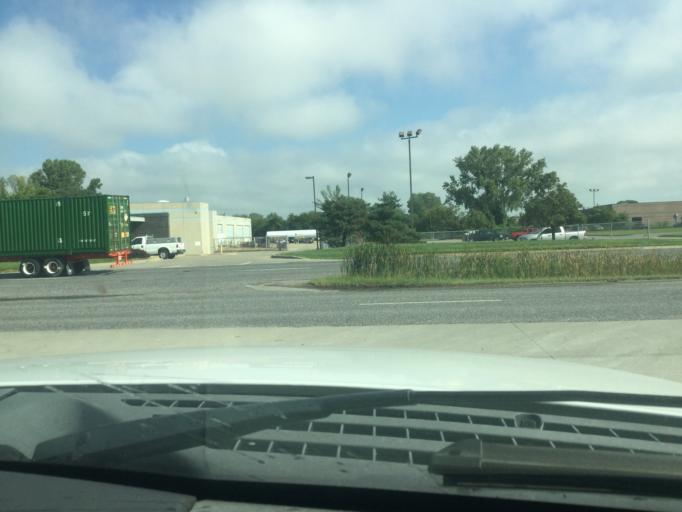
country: US
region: Missouri
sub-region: Clay County
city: North Kansas City
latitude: 39.1302
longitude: -94.5108
